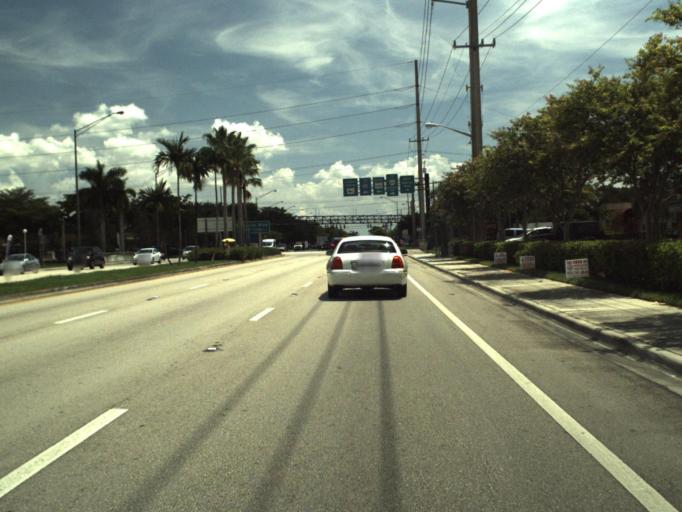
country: US
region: Florida
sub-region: Broward County
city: Plantation
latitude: 26.1510
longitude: -80.2573
